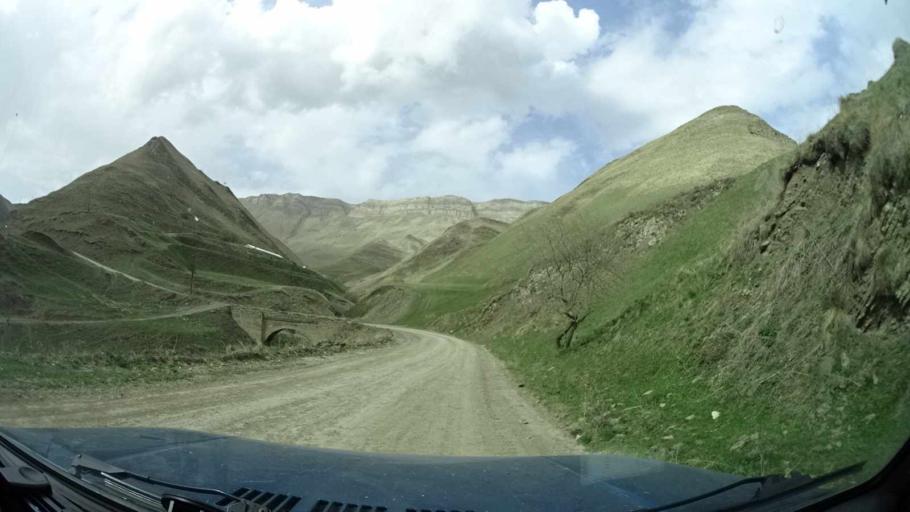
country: RU
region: Dagestan
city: Usisha
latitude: 42.1266
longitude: 47.3771
